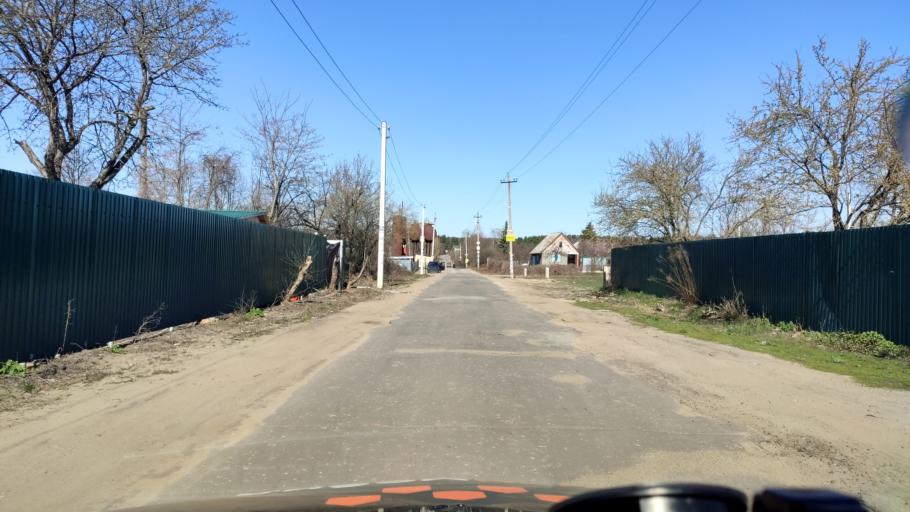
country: RU
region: Voronezj
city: Shilovo
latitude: 51.6003
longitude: 39.1435
